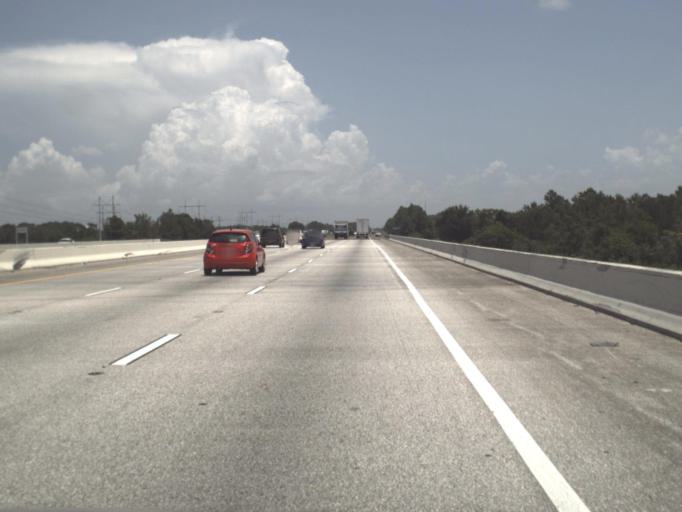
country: US
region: Florida
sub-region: Hillsborough County
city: Ruskin
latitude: 27.6674
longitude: -82.4316
